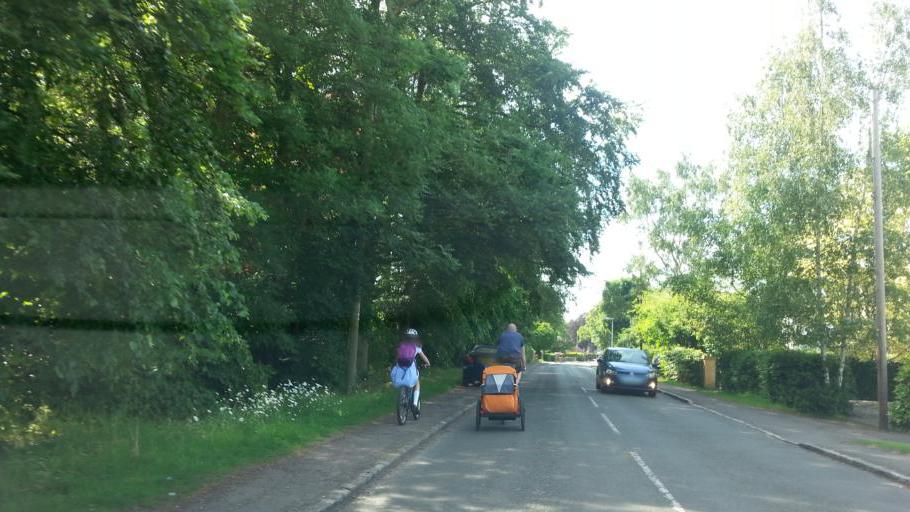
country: GB
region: England
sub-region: Cambridgeshire
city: Sawston
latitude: 52.1486
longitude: 0.1446
